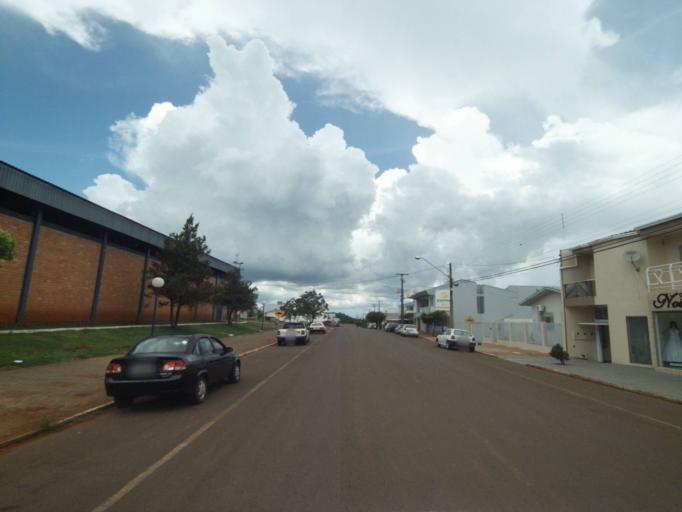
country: BR
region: Parana
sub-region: Guaraniacu
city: Guaraniacu
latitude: -25.1021
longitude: -52.8664
